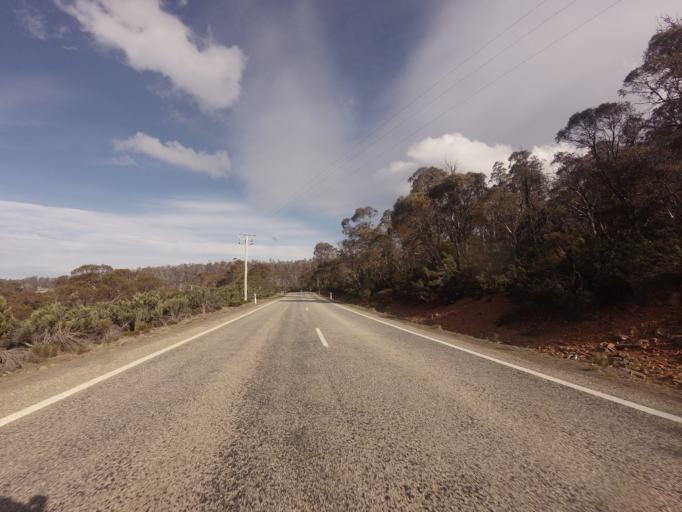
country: AU
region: Tasmania
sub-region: Meander Valley
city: Deloraine
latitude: -41.9850
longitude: 146.6794
